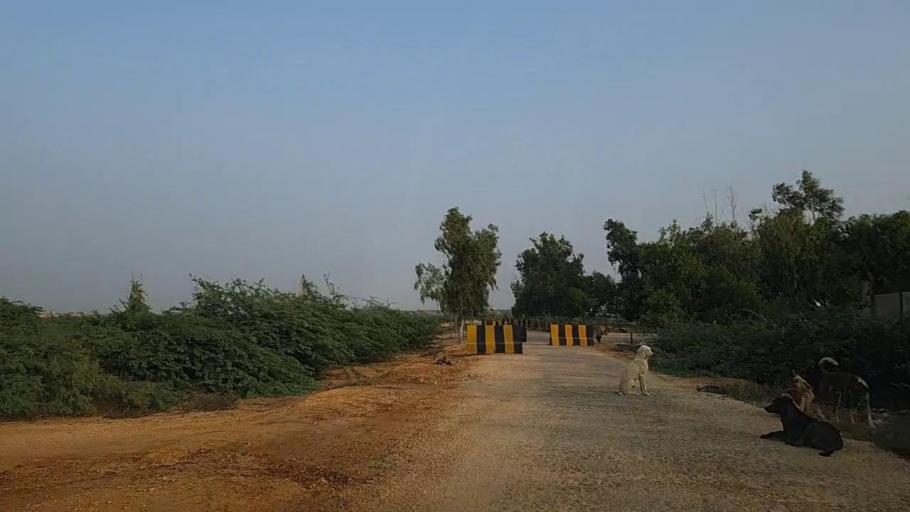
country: PK
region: Sindh
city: Thatta
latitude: 24.6902
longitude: 67.8476
